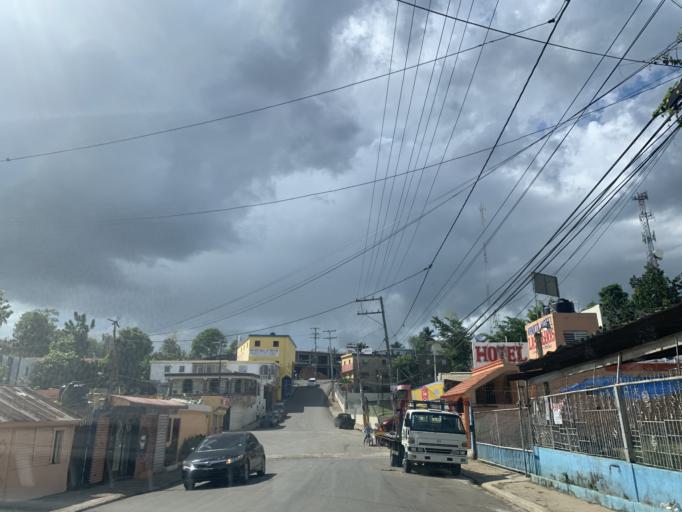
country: DO
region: Monte Plata
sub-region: Yamasa
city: Yamasa
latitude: 18.7740
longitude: -70.0248
